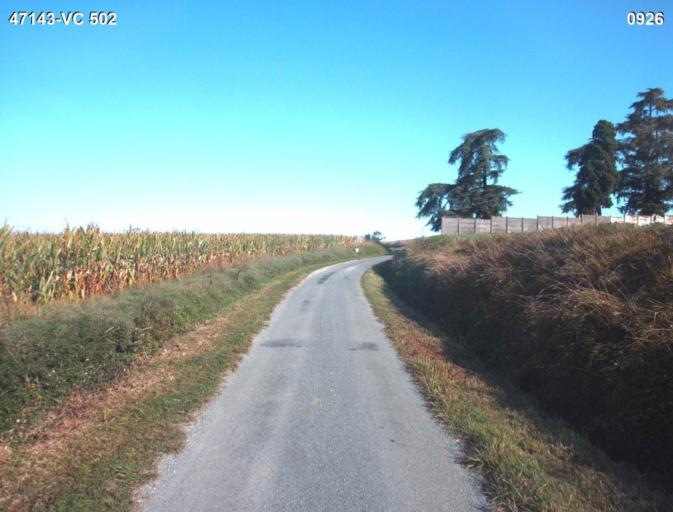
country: FR
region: Aquitaine
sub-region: Departement du Lot-et-Garonne
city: Vianne
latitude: 44.1718
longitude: 0.3271
